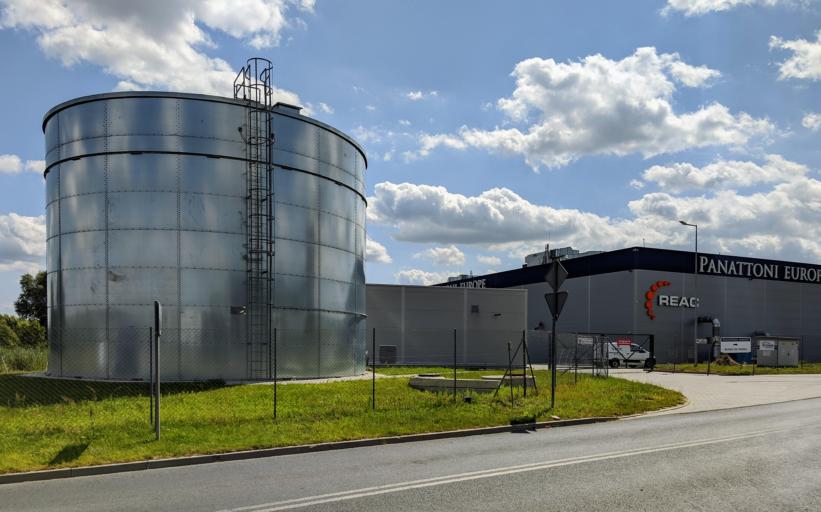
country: PL
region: Lubusz
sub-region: Powiat zielonogorski
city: Zabor
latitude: 51.9270
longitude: 15.6185
